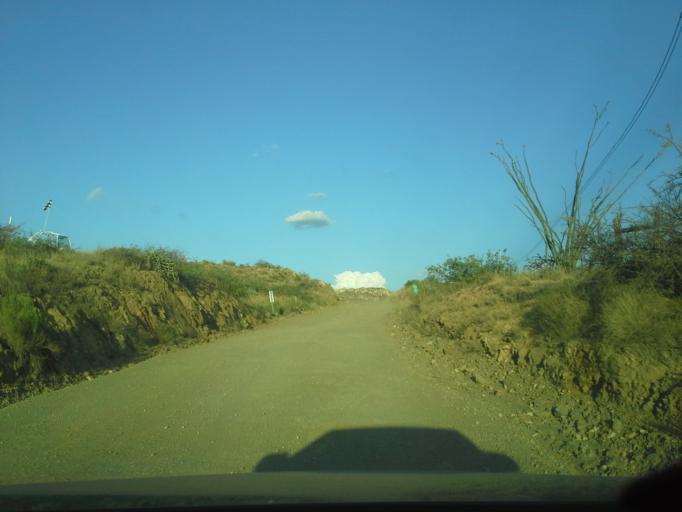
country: US
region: Arizona
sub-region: Yavapai County
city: Spring Valley
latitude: 34.2785
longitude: -112.2323
